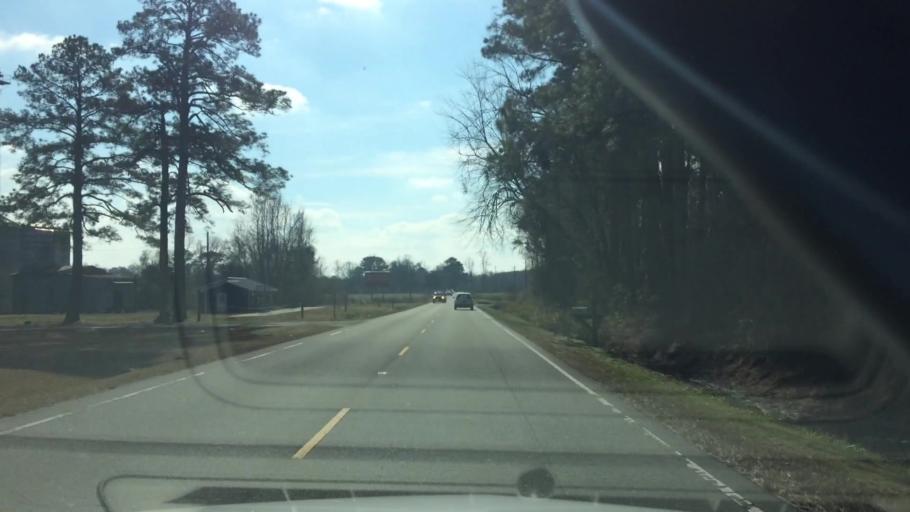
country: US
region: North Carolina
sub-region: Duplin County
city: Beulaville
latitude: 34.8608
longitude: -77.7958
